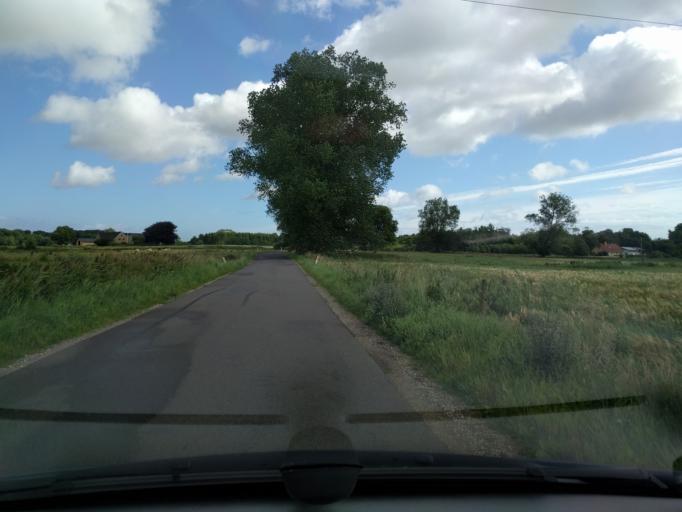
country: DK
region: South Denmark
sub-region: Kerteminde Kommune
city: Langeskov
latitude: 55.3841
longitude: 10.5794
